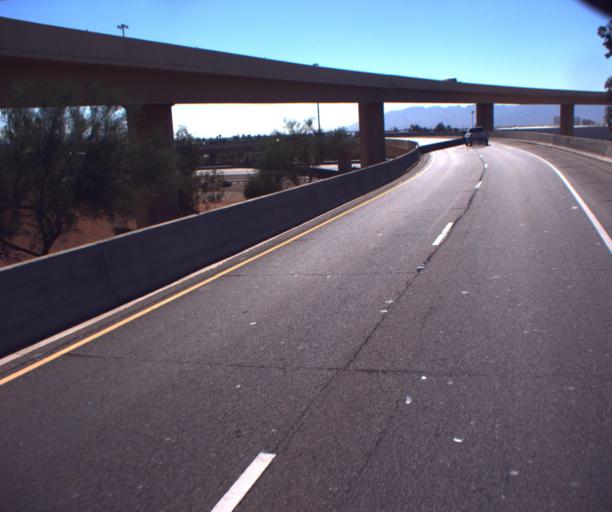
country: US
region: Arizona
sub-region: Maricopa County
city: Tolleson
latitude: 33.4637
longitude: -112.2688
